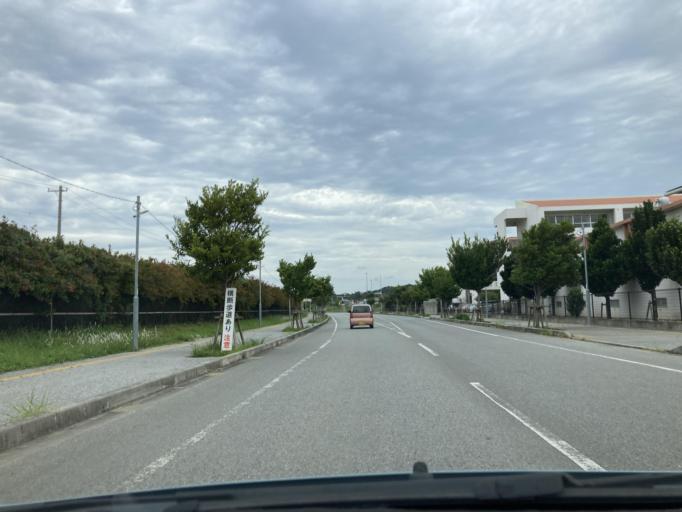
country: JP
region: Okinawa
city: Okinawa
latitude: 26.3951
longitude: 127.7410
